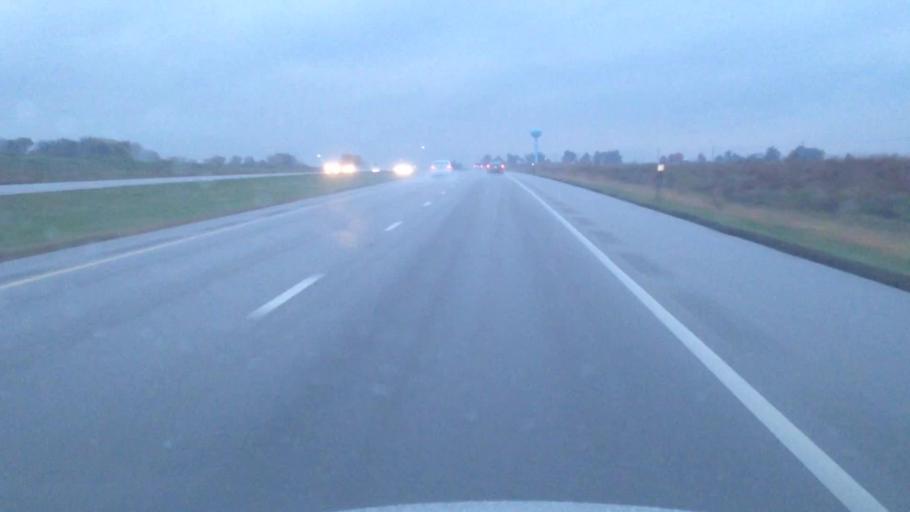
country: US
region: Kansas
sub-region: Douglas County
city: Baldwin City
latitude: 38.8467
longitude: -95.2667
